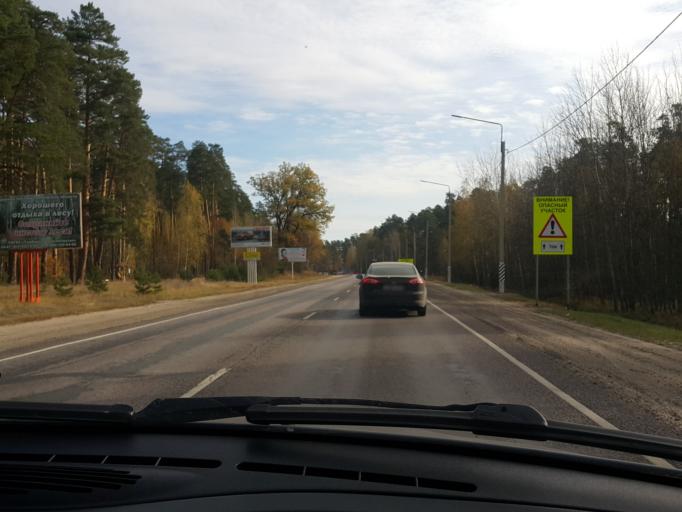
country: RU
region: Tambov
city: Donskoye
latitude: 52.7078
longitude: 41.5380
